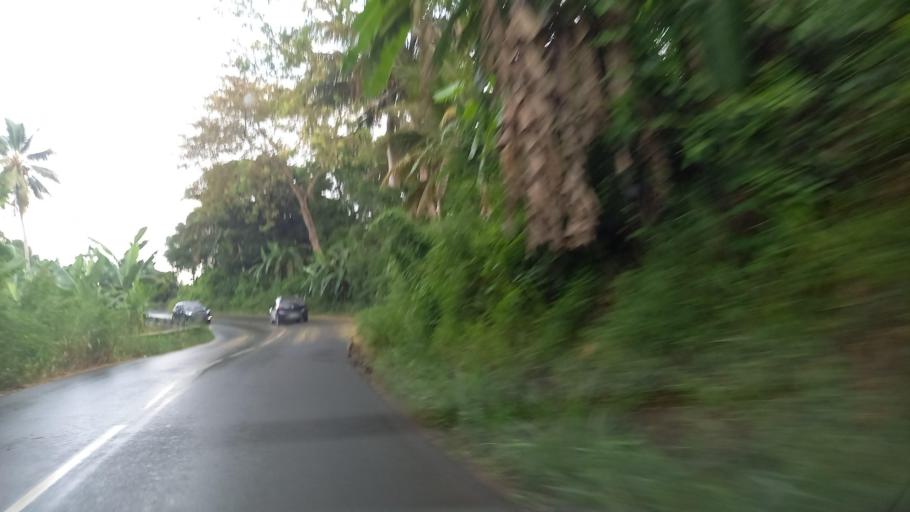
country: YT
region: Dembeni
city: Dembeni
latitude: -12.8394
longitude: 45.1632
